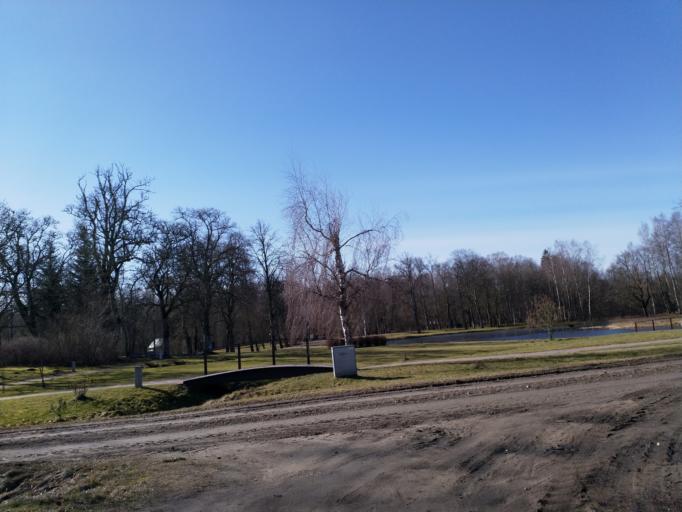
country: LV
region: Aizpute
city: Aizpute
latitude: 56.8337
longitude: 21.7758
